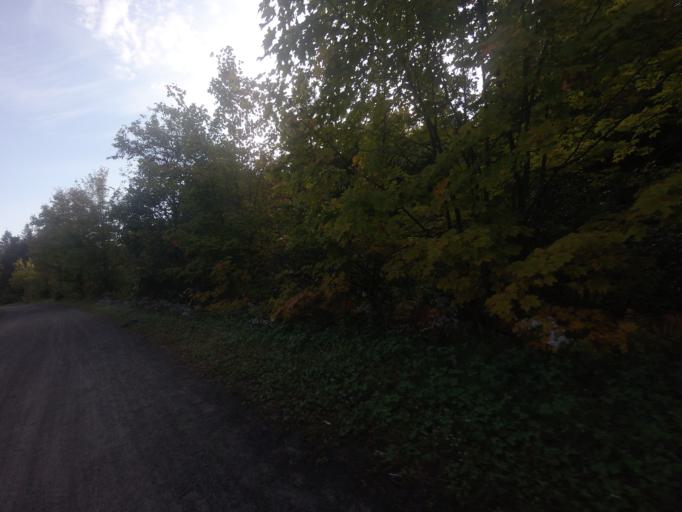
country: CA
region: Quebec
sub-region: Laurentides
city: Sainte-Adele
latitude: 45.9578
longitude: -74.1050
